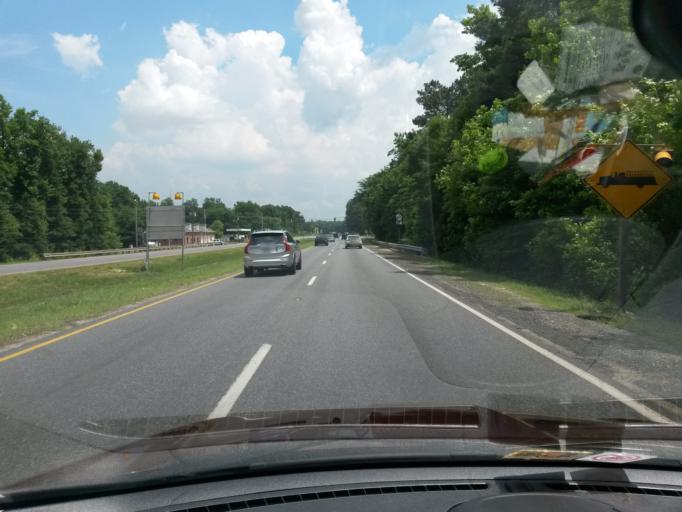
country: US
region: Virginia
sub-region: Chesterfield County
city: Enon
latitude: 37.3328
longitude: -77.3247
